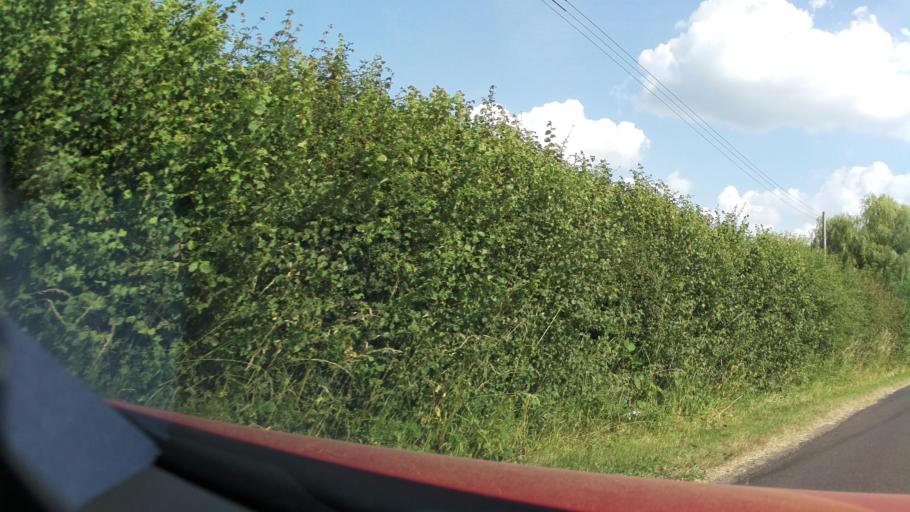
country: GB
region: England
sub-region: Wiltshire
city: Minety
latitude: 51.6297
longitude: -1.9738
